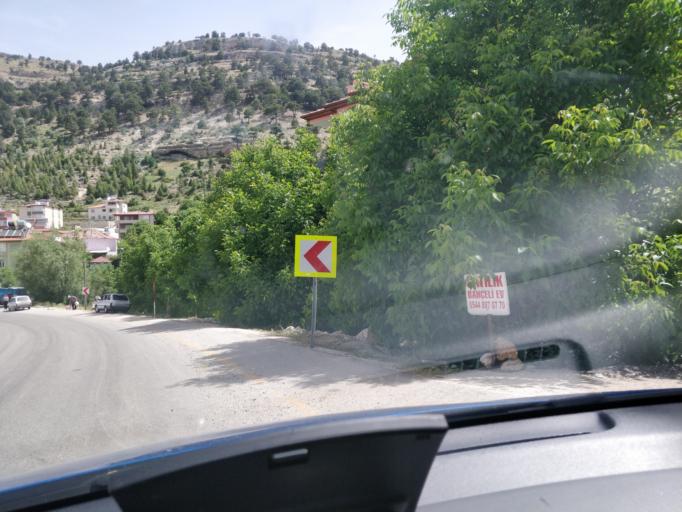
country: TR
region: Karaman
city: Bucakkisla
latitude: 36.8826
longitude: 33.2814
